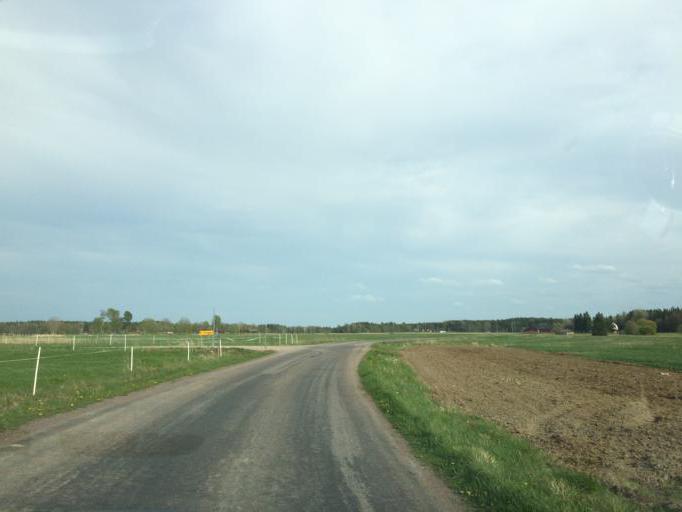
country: SE
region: Vaestmanland
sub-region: Hallstahammars Kommun
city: Hallstahammar
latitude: 59.5988
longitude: 16.1338
